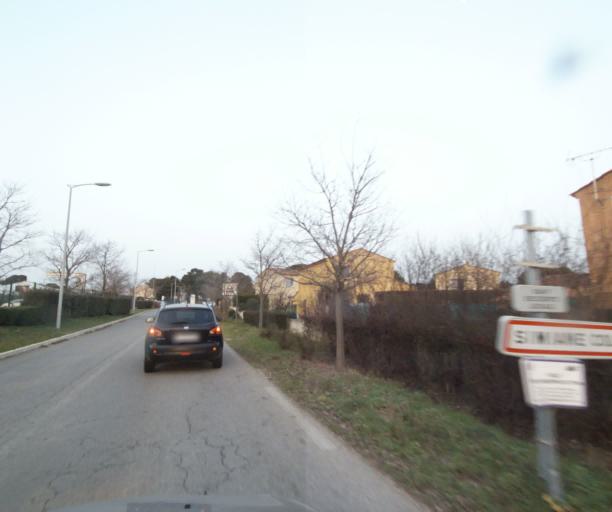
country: FR
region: Provence-Alpes-Cote d'Azur
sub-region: Departement des Bouches-du-Rhone
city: Simiane-Collongue
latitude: 43.4337
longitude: 5.4246
